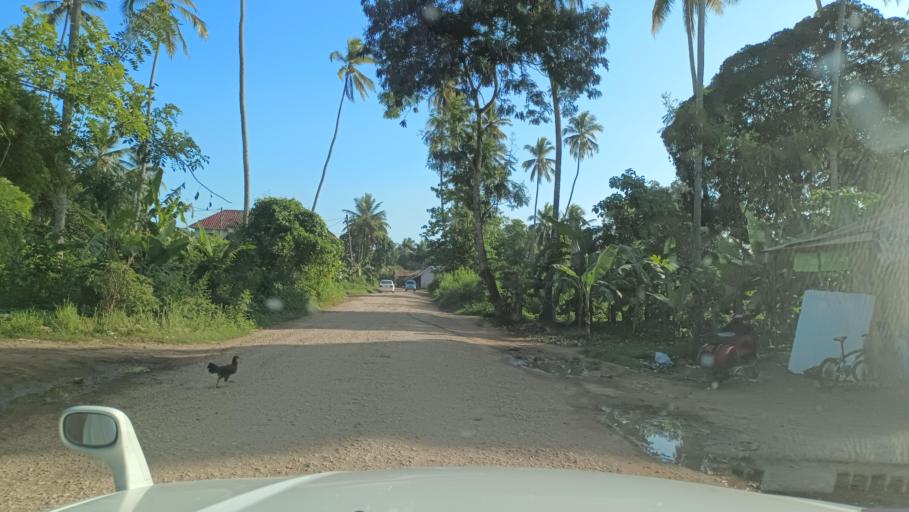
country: TZ
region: Zanzibar Urban/West
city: Zanzibar
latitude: -6.2337
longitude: 39.2194
